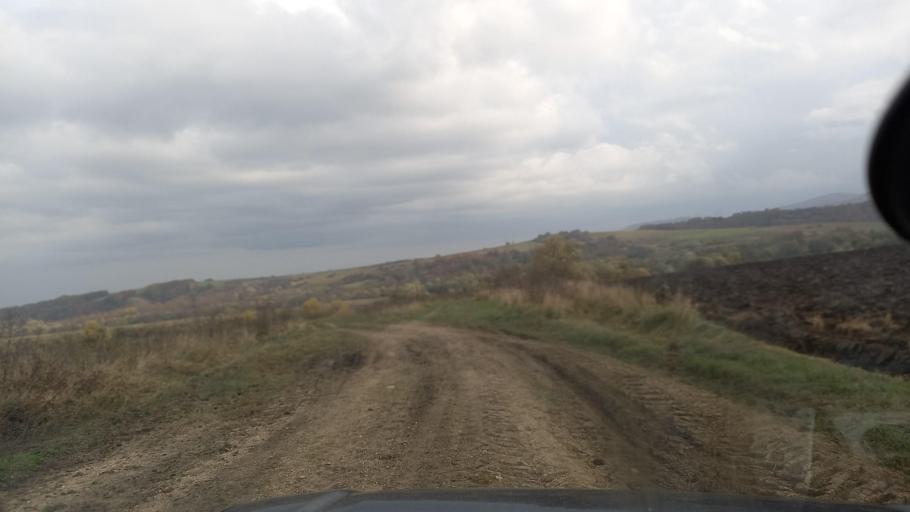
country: RU
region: Krasnodarskiy
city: Gubskaya
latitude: 44.3074
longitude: 40.5491
